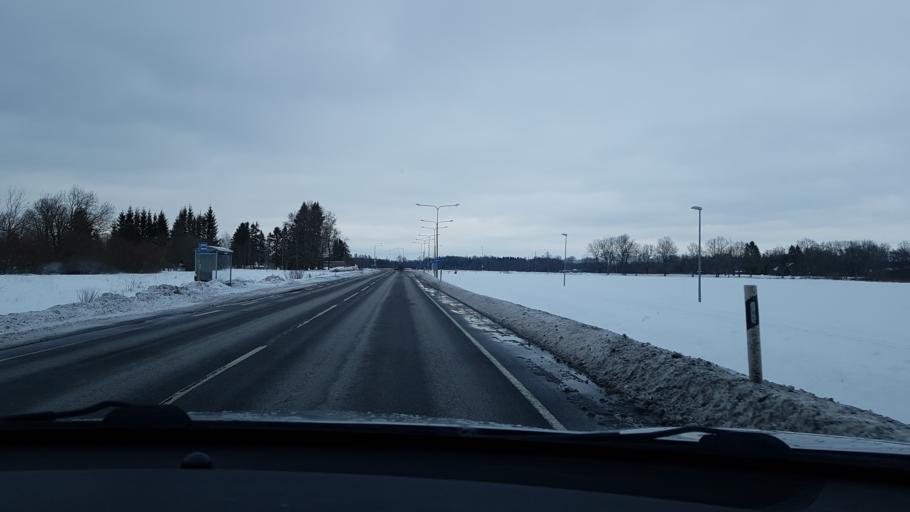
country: EE
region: Jaervamaa
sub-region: Paide linn
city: Paide
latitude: 58.9374
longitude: 25.6372
